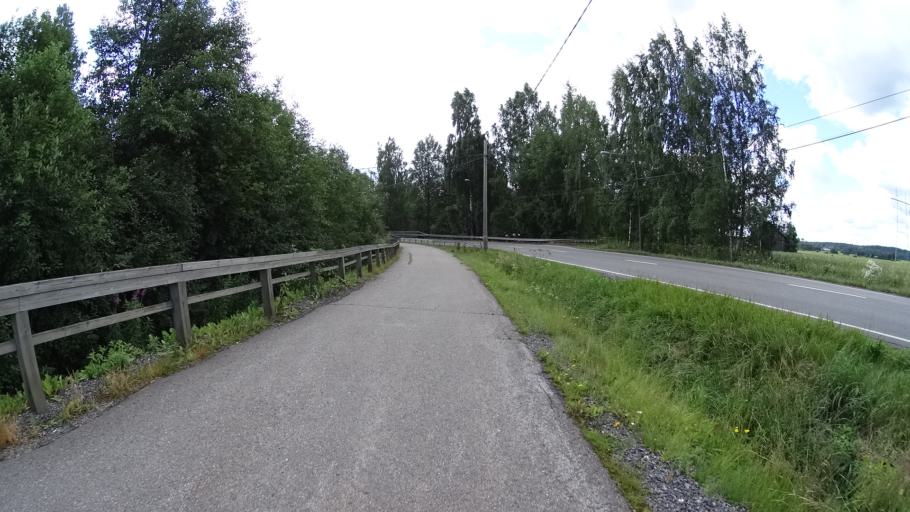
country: FI
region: Uusimaa
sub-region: Helsinki
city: Tuusula
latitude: 60.3395
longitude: 24.9204
